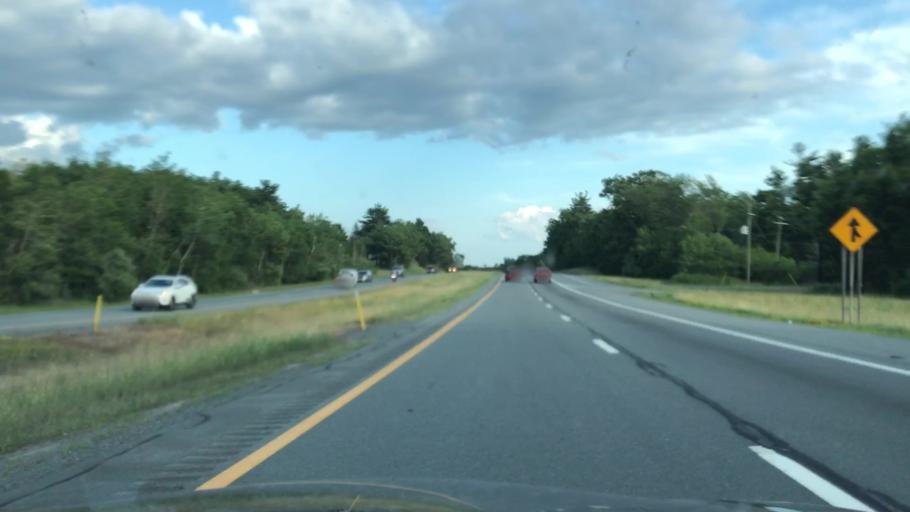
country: US
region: New York
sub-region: Sullivan County
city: Rock Hill
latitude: 41.6150
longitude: -74.5752
